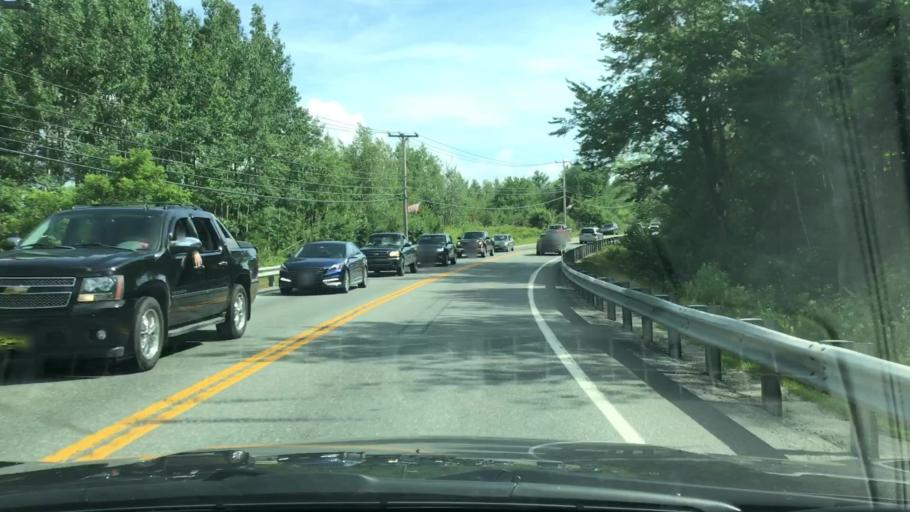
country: US
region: Maine
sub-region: Hancock County
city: Trenton
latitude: 44.4825
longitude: -68.3657
